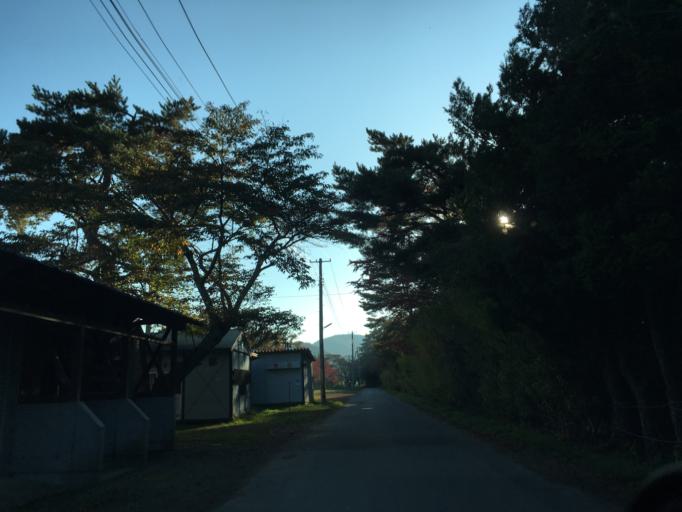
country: JP
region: Fukushima
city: Inawashiro
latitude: 37.4205
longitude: 140.1305
